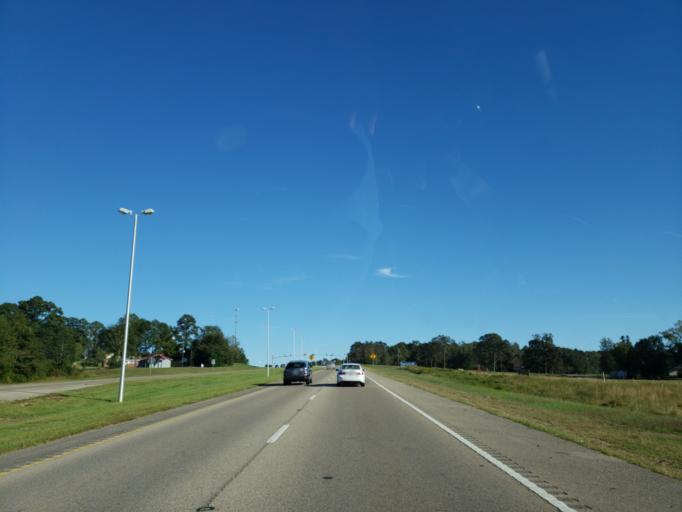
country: US
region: Mississippi
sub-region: Forrest County
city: Petal
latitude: 31.3551
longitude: -89.2552
